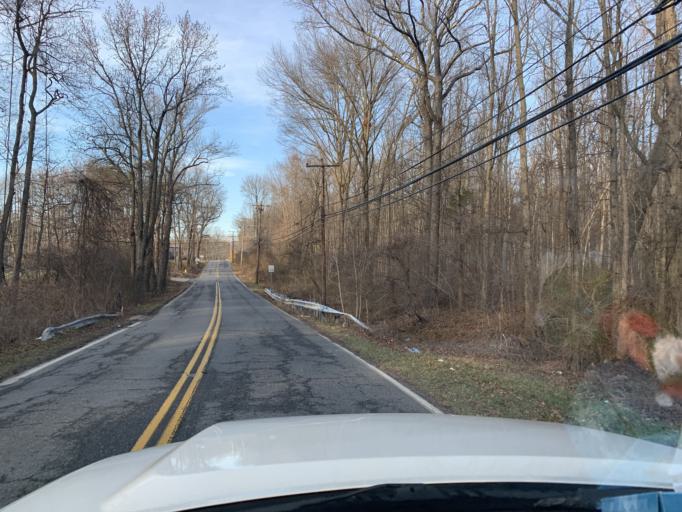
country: US
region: Maryland
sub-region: Anne Arundel County
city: Jessup
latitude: 39.1438
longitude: -76.7576
